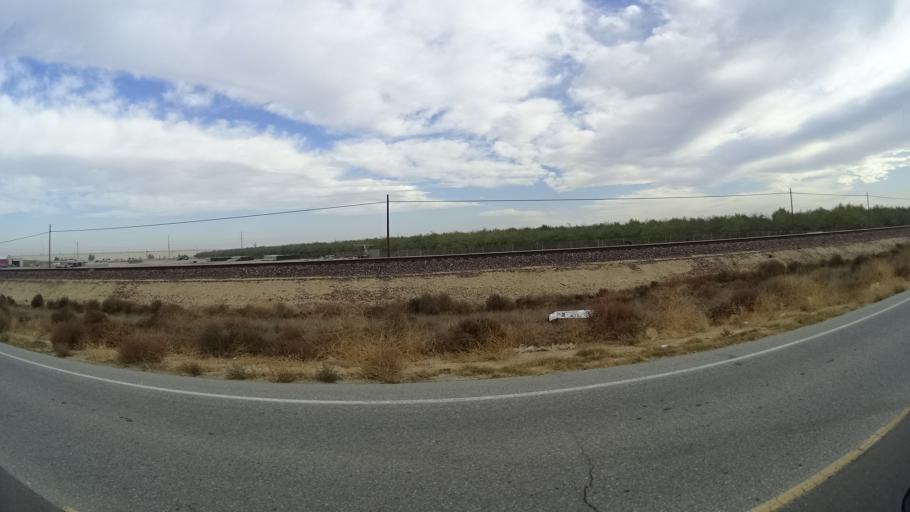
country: US
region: California
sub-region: Kern County
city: Rosedale
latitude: 35.4382
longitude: -119.1950
